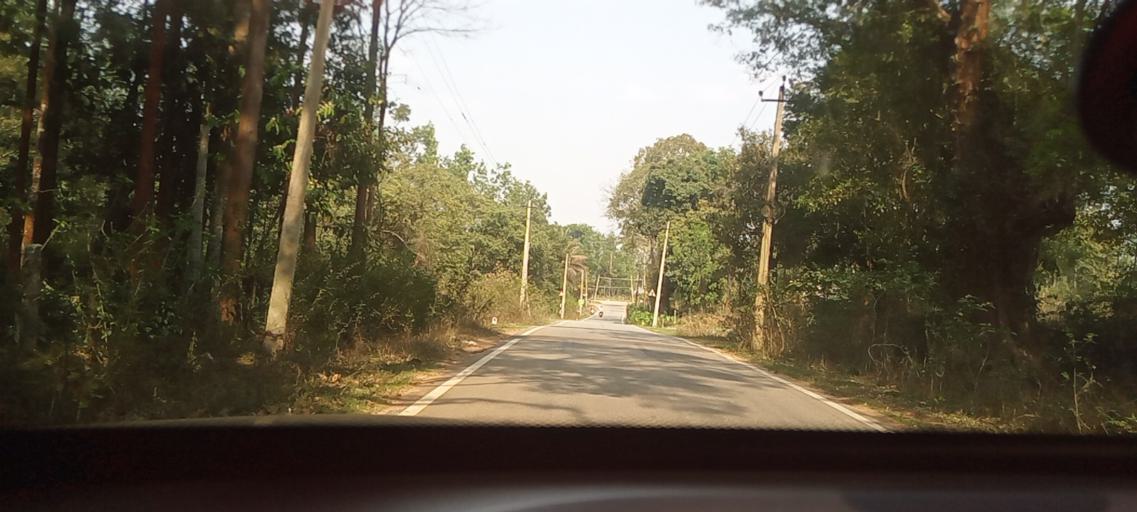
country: IN
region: Karnataka
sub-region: Hassan
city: Belur
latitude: 13.1892
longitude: 75.7893
